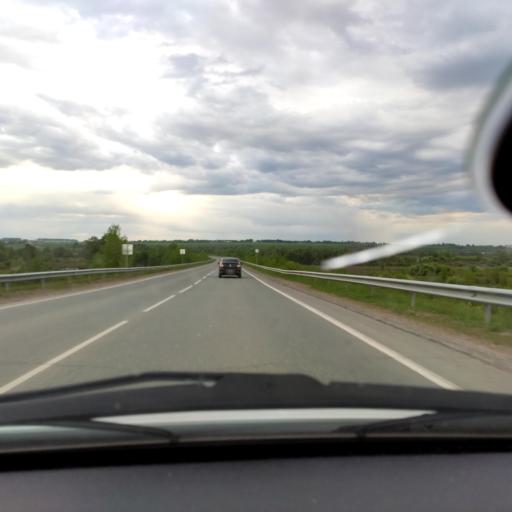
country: RU
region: Bashkortostan
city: Dyurtyuli
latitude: 55.5270
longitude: 54.8443
